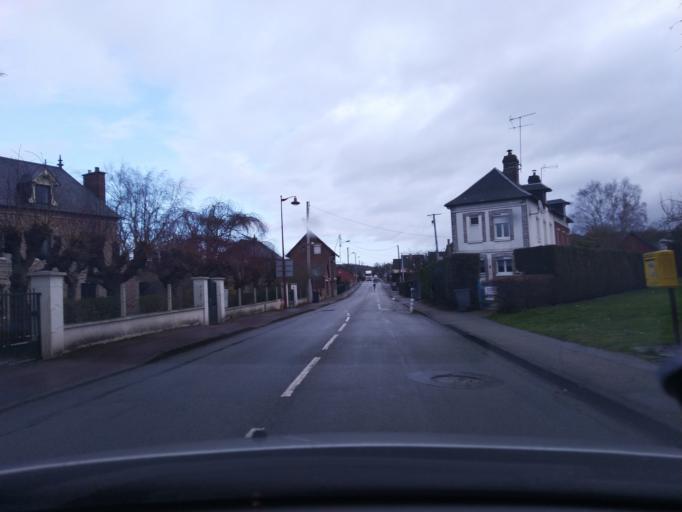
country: FR
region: Haute-Normandie
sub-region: Departement de la Seine-Maritime
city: Duclair
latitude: 49.4865
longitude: 0.8789
